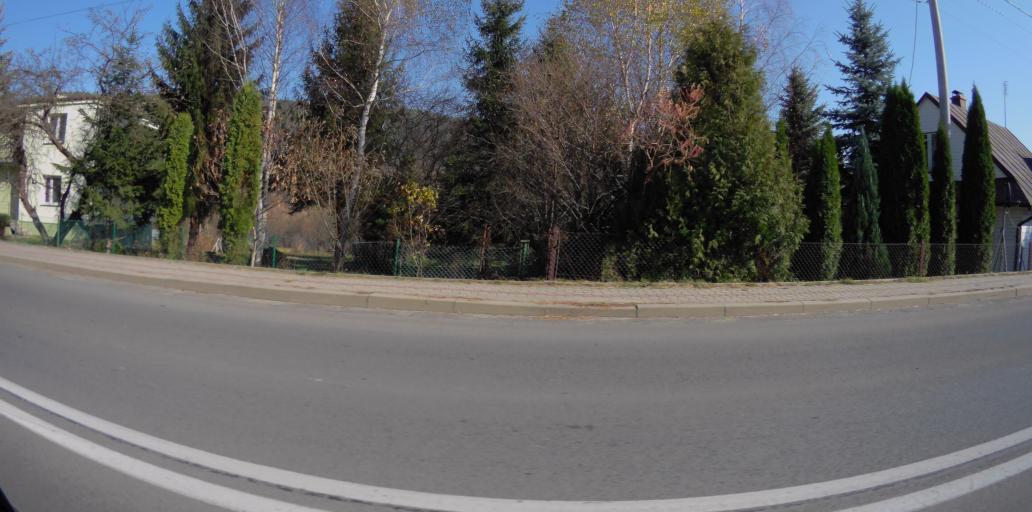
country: PL
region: Subcarpathian Voivodeship
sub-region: Powiat bieszczadzki
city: Ustrzyki Dolne
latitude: 49.4250
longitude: 22.6074
